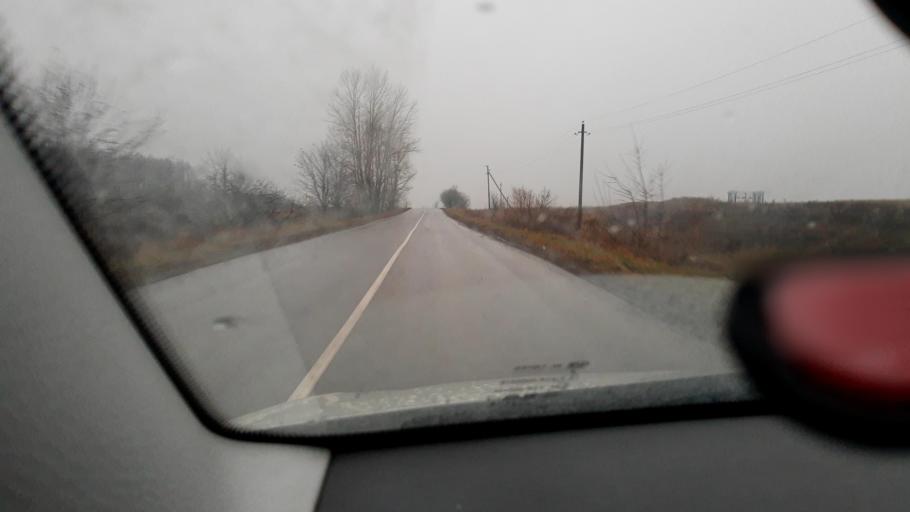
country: RU
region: Bashkortostan
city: Iglino
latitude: 54.8999
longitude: 56.2607
